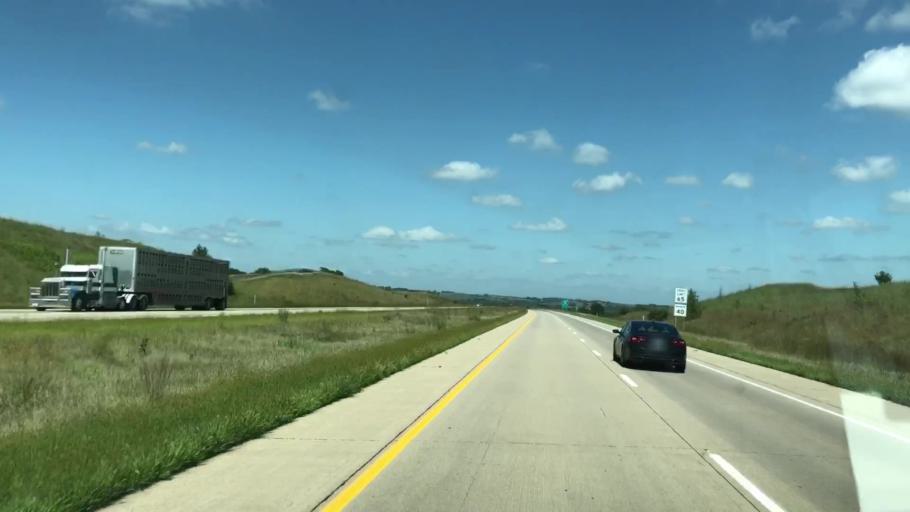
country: US
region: Iowa
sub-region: Woodbury County
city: Sioux City
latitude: 42.5281
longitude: -96.3388
